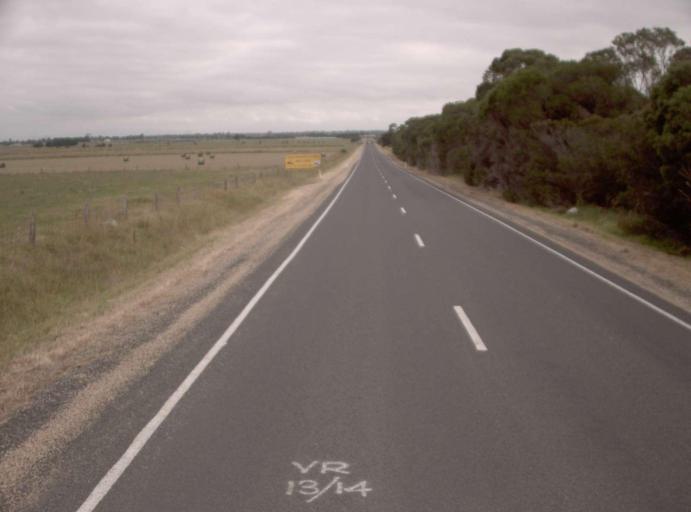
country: AU
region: Victoria
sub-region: Wellington
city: Sale
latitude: -38.0916
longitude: 146.9865
